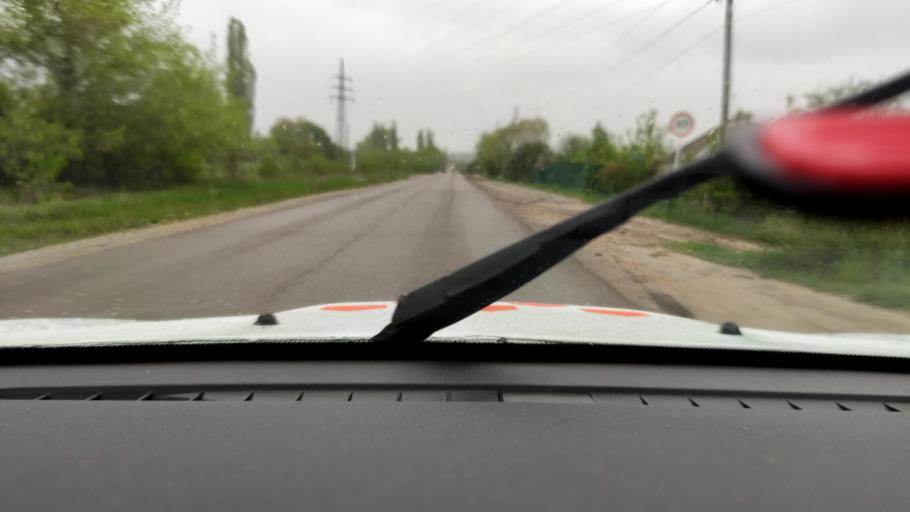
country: RU
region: Voronezj
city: Strelitsa
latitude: 51.6210
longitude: 38.9103
